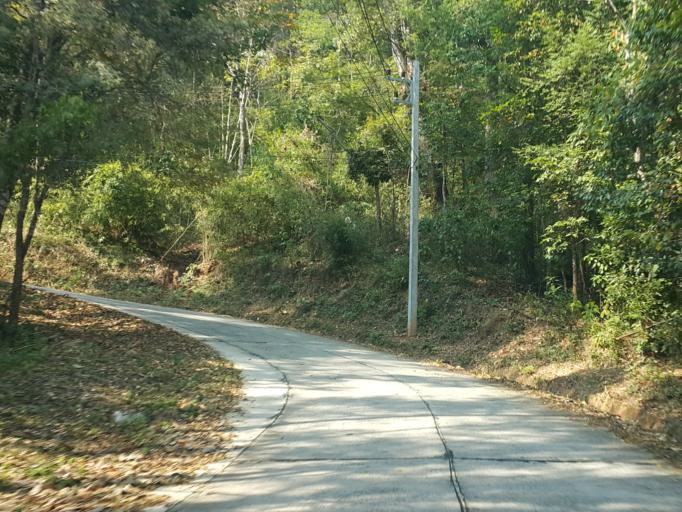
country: TH
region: Chiang Mai
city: Mae Taeng
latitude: 19.0209
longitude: 98.8003
